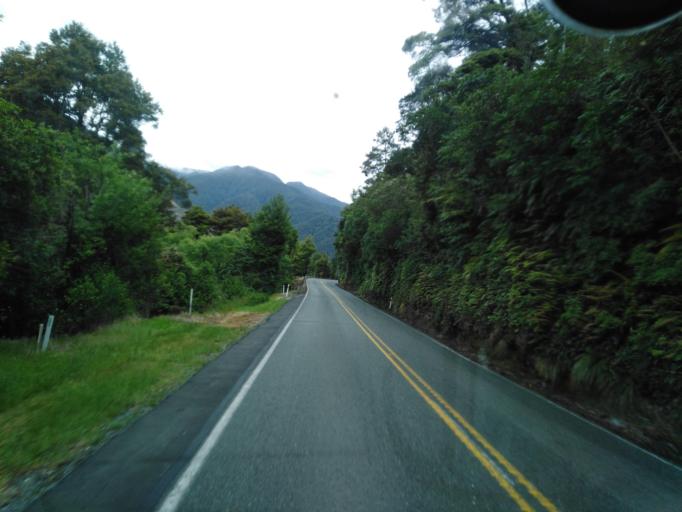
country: NZ
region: Tasman
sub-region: Tasman District
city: Wakefield
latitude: -41.7106
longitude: 172.5720
